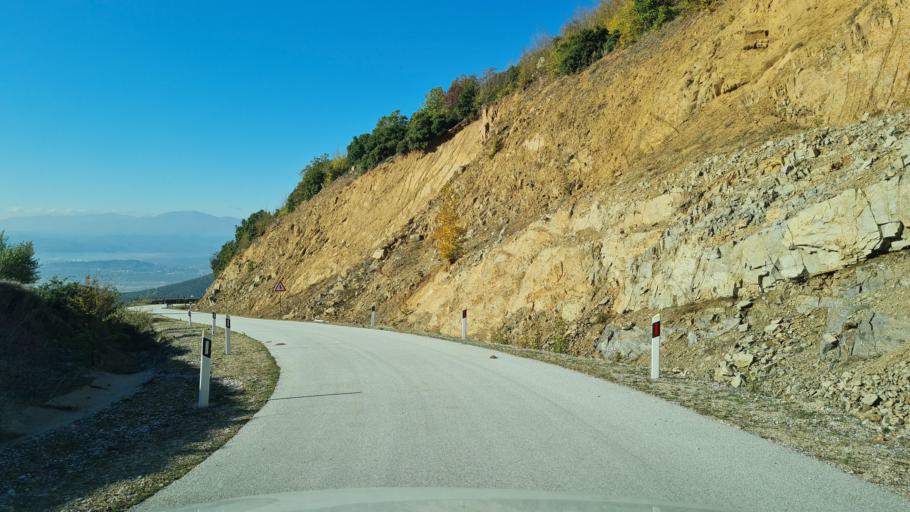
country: MK
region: Bogdanci
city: Bogdanci
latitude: 41.2251
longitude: 22.5589
